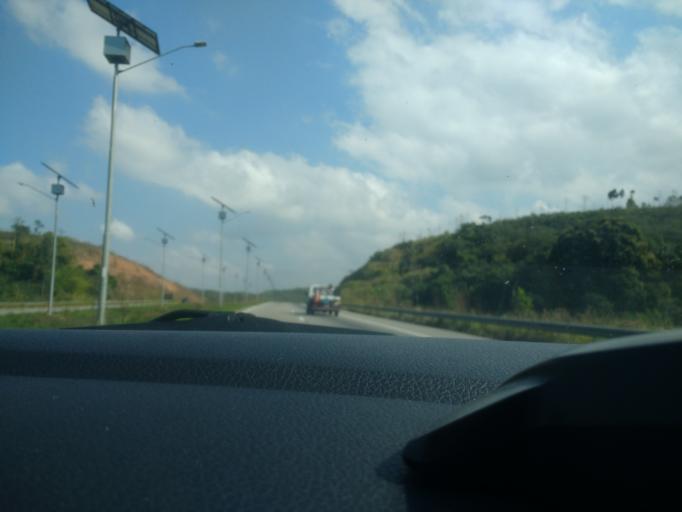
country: BR
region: Rio de Janeiro
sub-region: Queimados
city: Queimados
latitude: -22.6876
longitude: -43.5127
